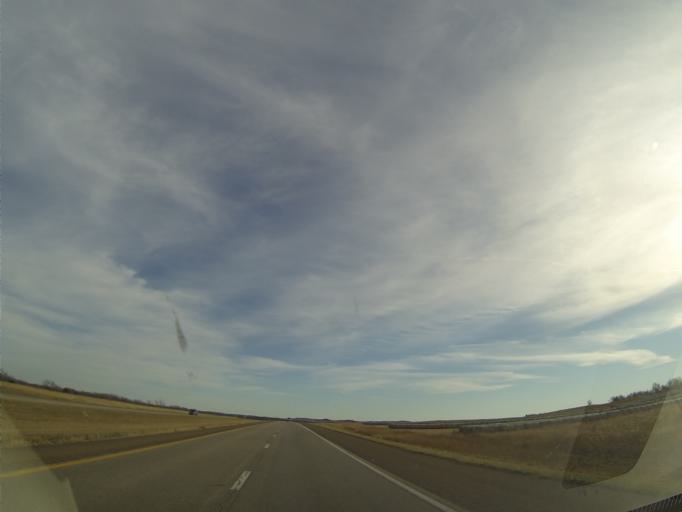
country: US
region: Kansas
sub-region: Ottawa County
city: Minneapolis
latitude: 39.0392
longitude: -97.6480
